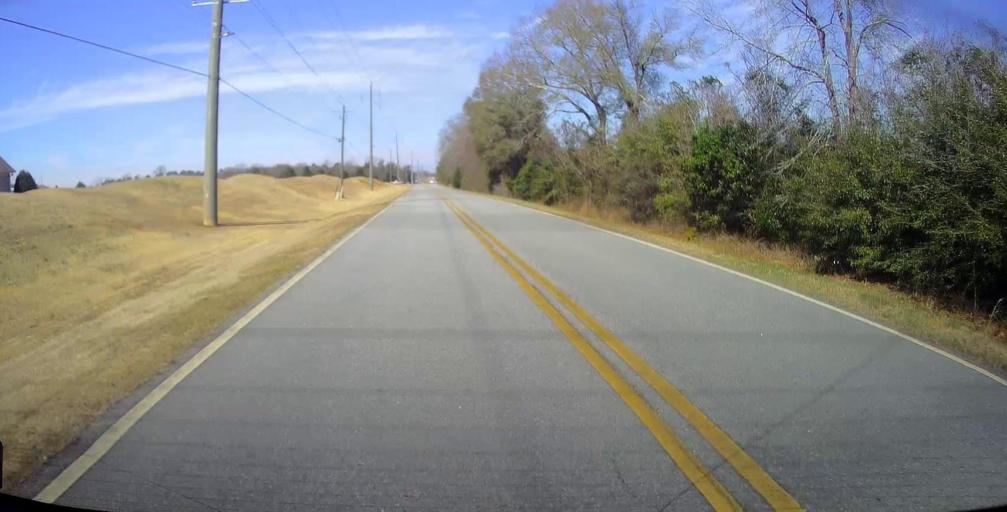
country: US
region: Georgia
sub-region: Houston County
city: Perry
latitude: 32.4745
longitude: -83.7590
